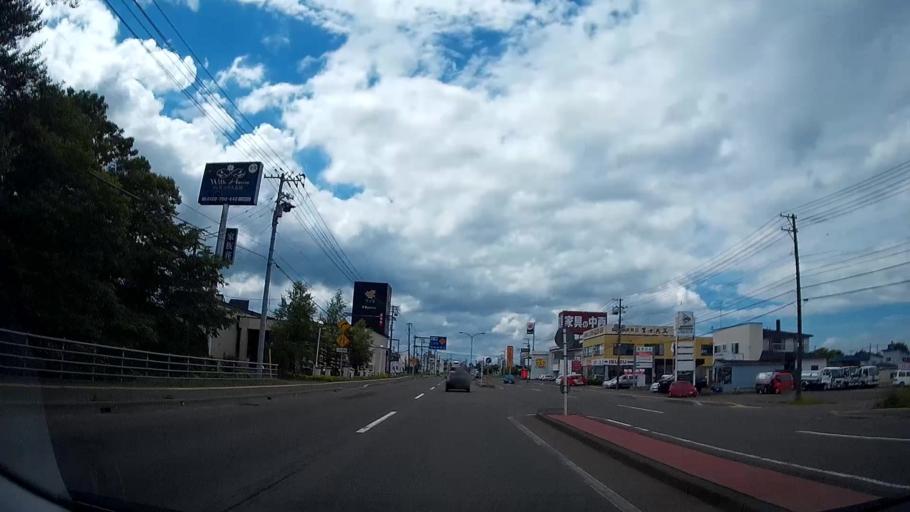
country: JP
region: Hokkaido
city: Chitose
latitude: 42.8702
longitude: 141.5883
